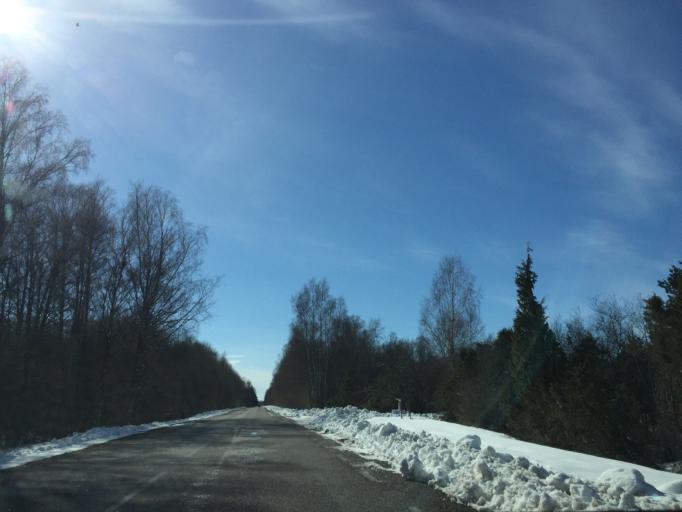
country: EE
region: Saare
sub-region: Orissaare vald
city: Orissaare
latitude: 58.3978
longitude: 22.9774
